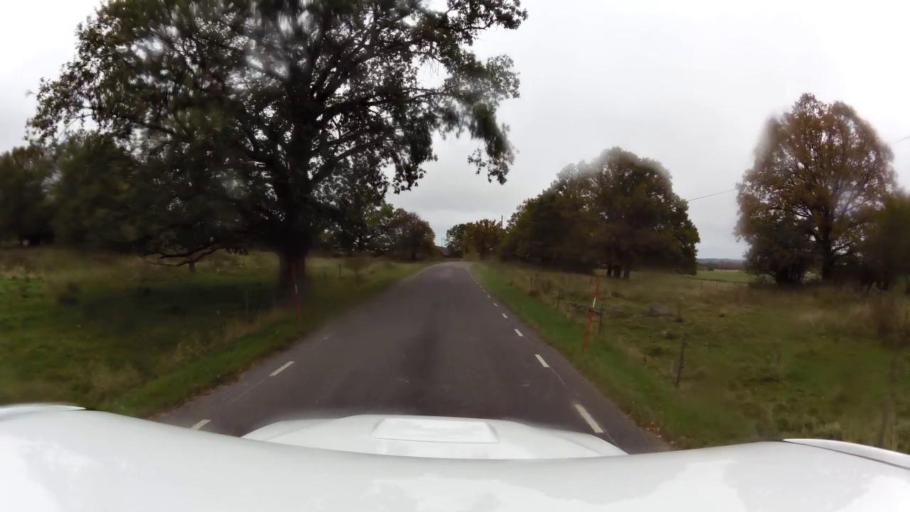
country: SE
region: OEstergoetland
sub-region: Linkopings Kommun
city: Linghem
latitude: 58.4766
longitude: 15.7588
